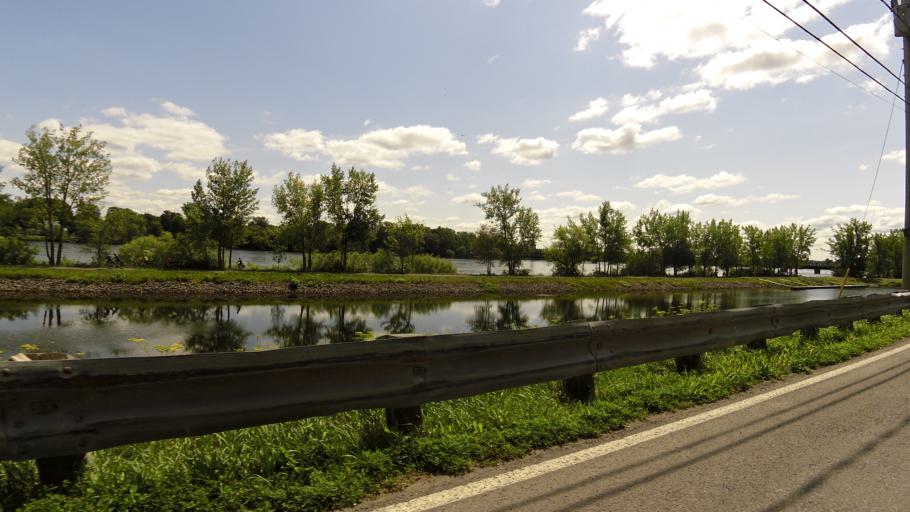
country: CA
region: Quebec
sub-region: Monteregie
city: Saint-Jean-sur-Richelieu
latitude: 45.3135
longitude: -73.2525
